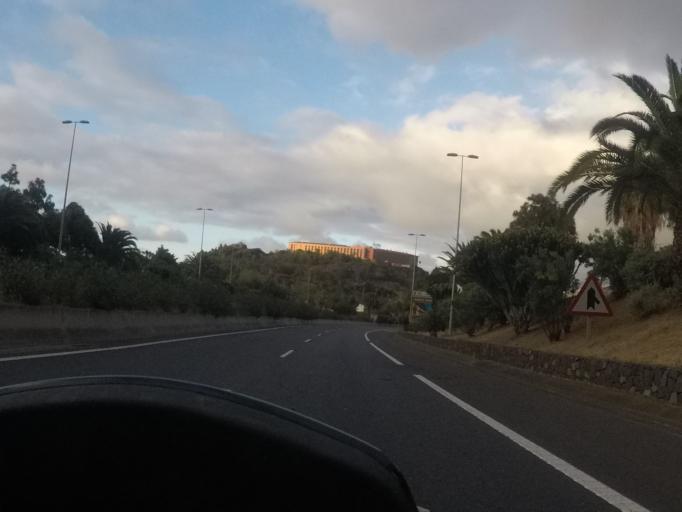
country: ES
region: Canary Islands
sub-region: Provincia de Santa Cruz de Tenerife
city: Puerto de la Cruz
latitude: 28.3958
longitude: -16.5505
